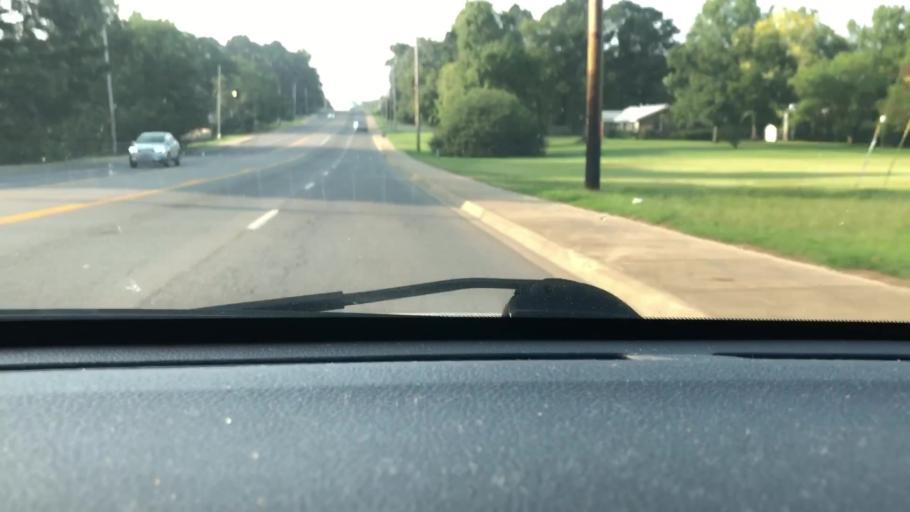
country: US
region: Arkansas
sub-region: Saline County
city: Bryant
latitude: 34.6069
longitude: -92.4920
